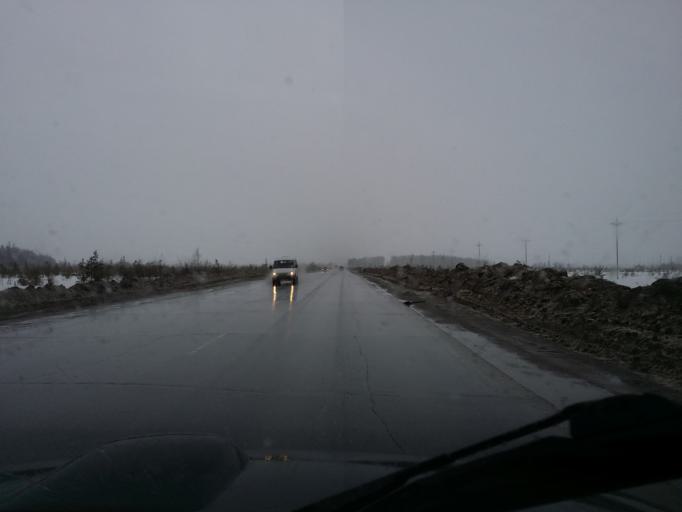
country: RU
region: Khanty-Mansiyskiy Avtonomnyy Okrug
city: Izluchinsk
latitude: 60.9602
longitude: 76.7418
